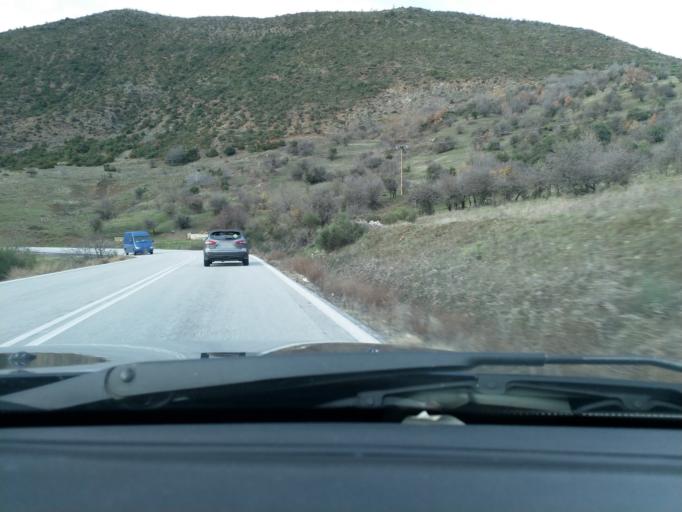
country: GR
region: Thessaly
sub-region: Trikala
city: Kastraki
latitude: 39.7555
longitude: 21.4906
